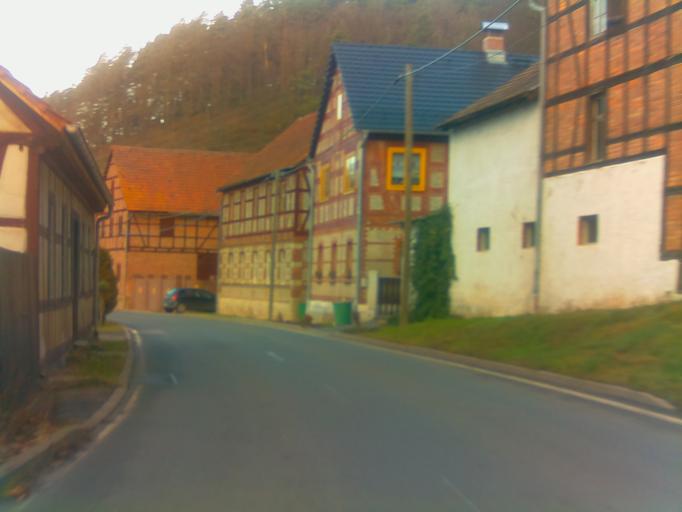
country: DE
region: Thuringia
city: Unterwellenborn
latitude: 50.6914
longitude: 11.4058
